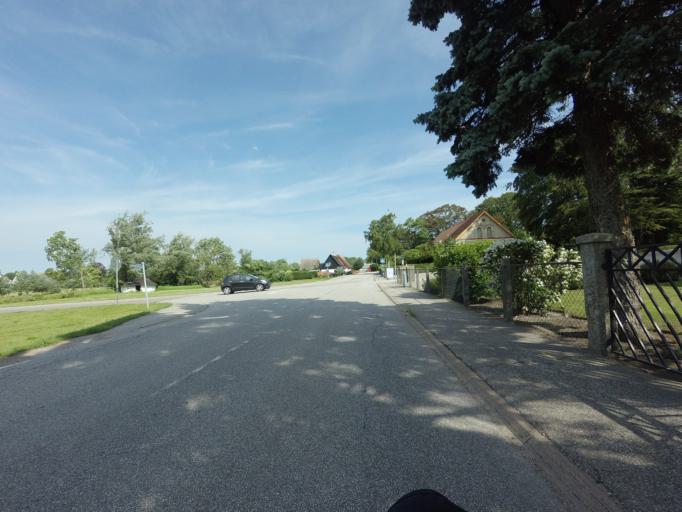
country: SE
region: Skane
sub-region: Vellinge Kommun
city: Vellinge
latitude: 55.5013
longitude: 13.0311
